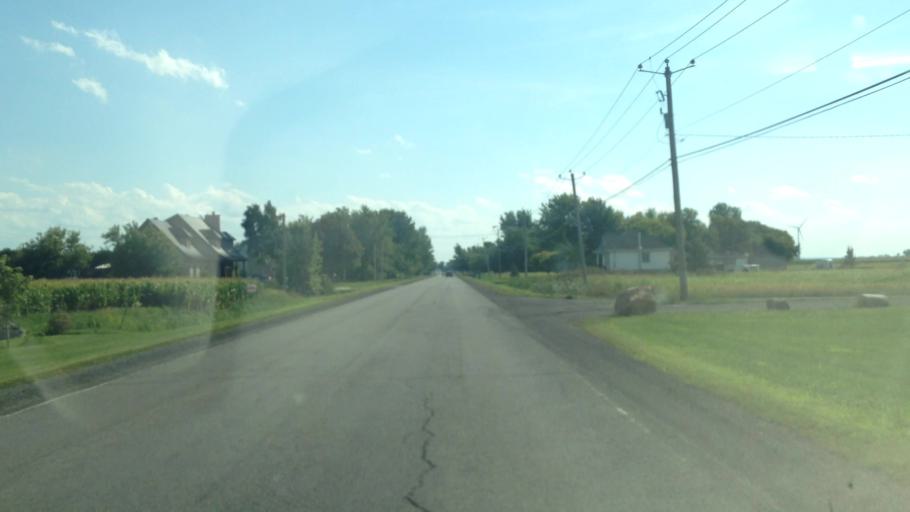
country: CA
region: Quebec
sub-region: Monteregie
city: Mercier
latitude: 45.2837
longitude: -73.6886
